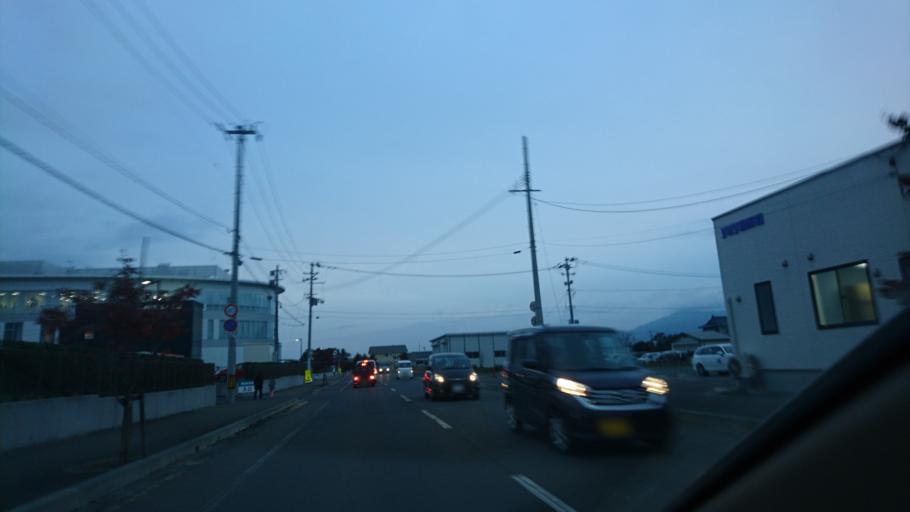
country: JP
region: Iwate
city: Morioka-shi
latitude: 39.6715
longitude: 141.1319
